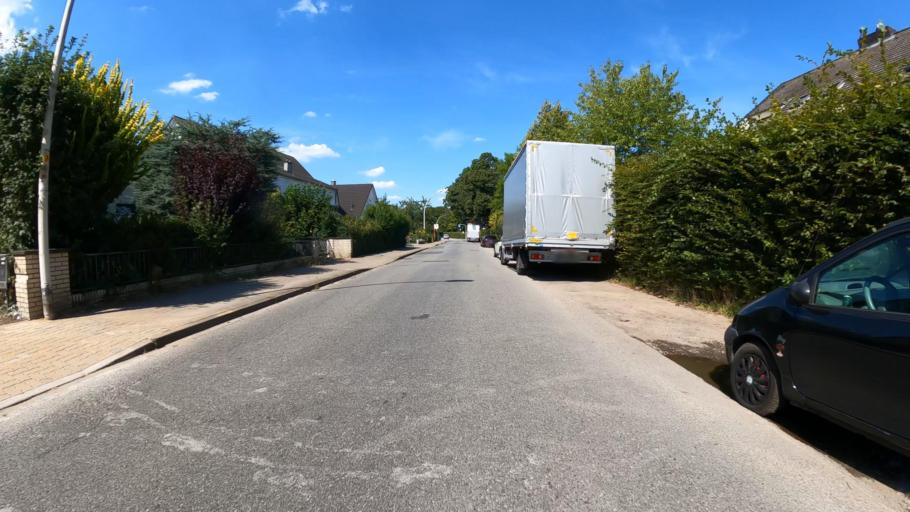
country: DE
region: Schleswig-Holstein
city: Halstenbek
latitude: 53.6173
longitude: 9.8719
